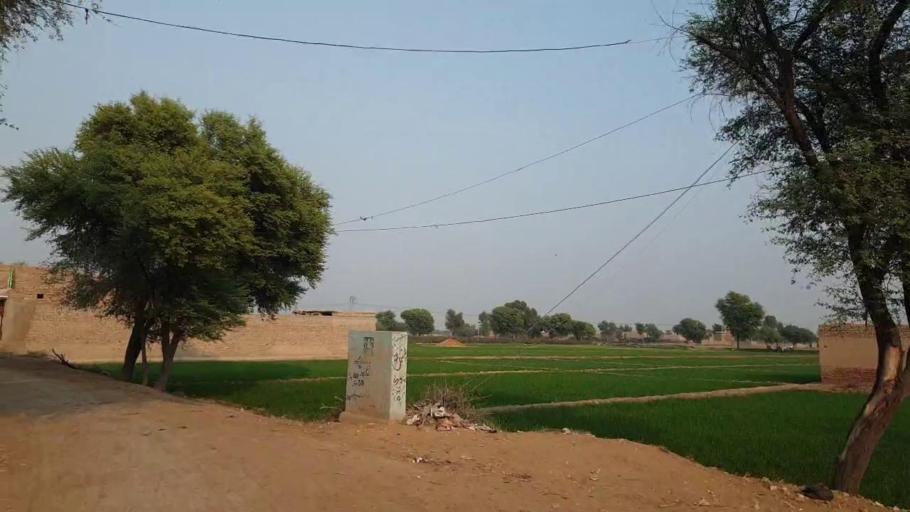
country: PK
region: Sindh
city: Bhan
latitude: 26.4951
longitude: 67.7493
